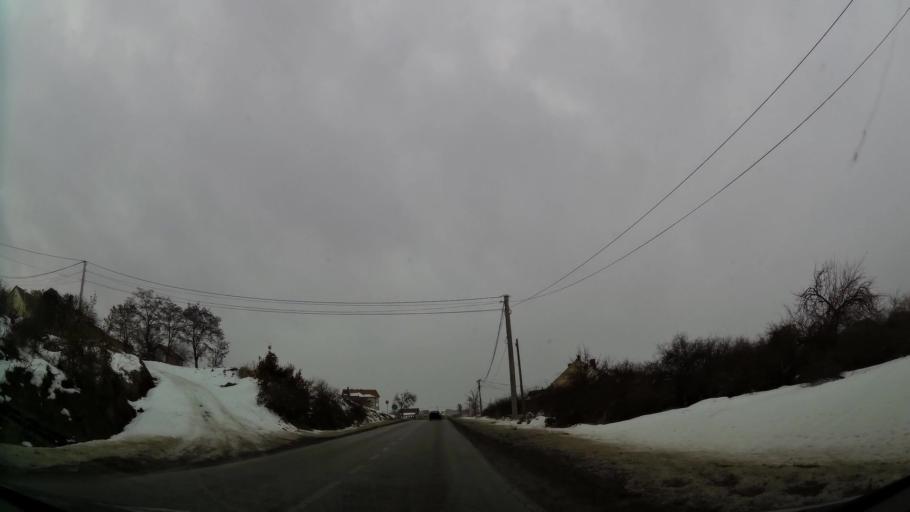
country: XK
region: Pristina
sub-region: Komuna e Prishtines
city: Pristina
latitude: 42.7242
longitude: 21.1453
